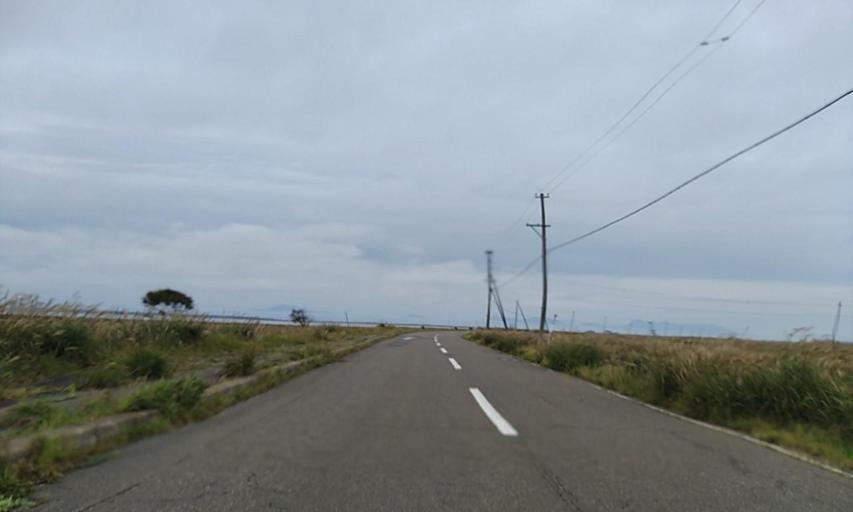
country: JP
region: Hokkaido
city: Shibetsu
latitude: 43.5704
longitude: 145.3457
